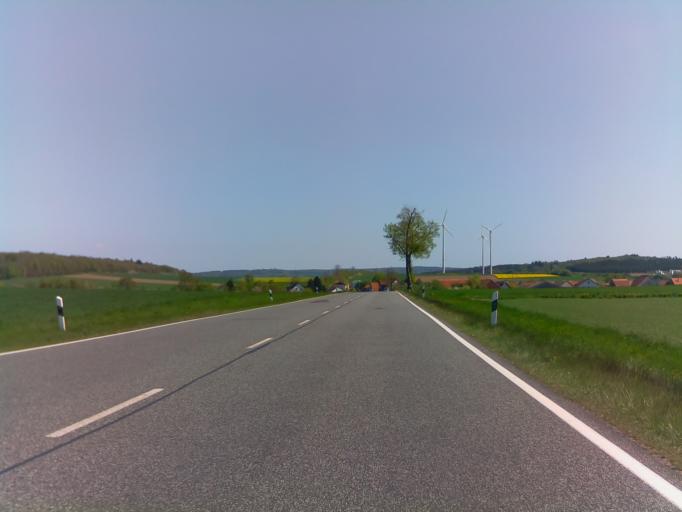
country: DE
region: Hesse
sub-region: Regierungsbezirk Giessen
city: Lauterbach
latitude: 50.6813
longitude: 9.3473
